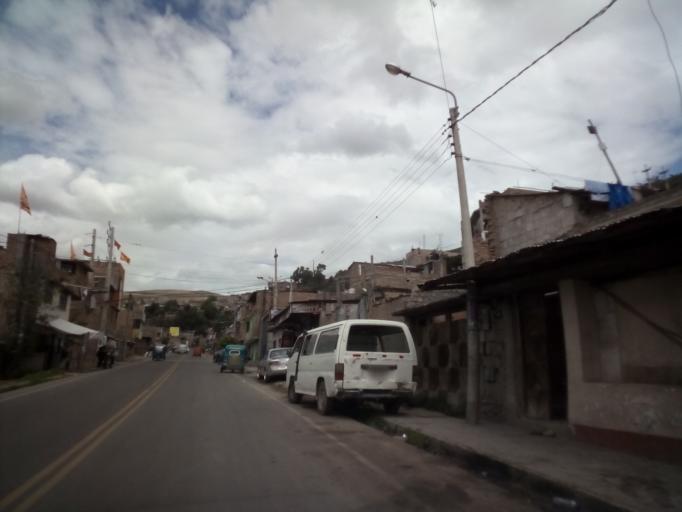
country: PE
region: Ayacucho
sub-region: Provincia de Huamanga
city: Ayacucho
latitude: -13.1532
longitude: -74.2377
